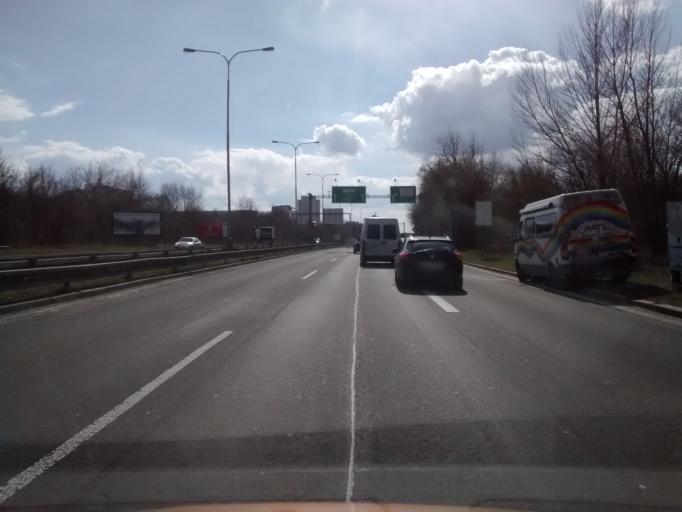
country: CZ
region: Praha
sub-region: Praha 9
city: Strizkov
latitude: 50.1314
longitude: 14.4892
